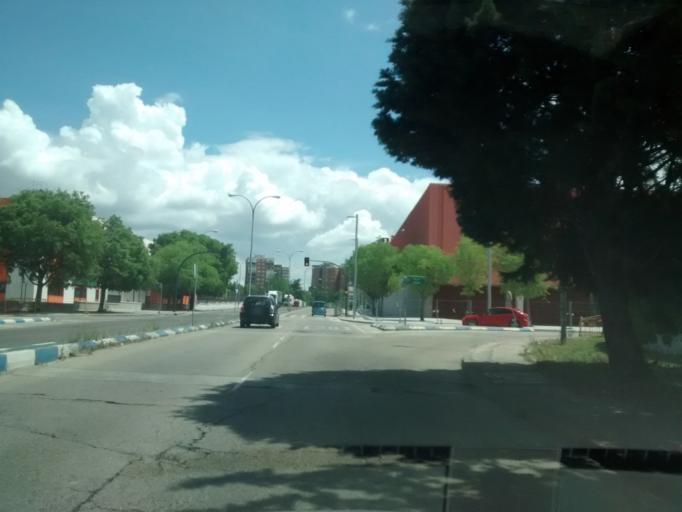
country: ES
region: Madrid
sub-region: Provincia de Madrid
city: Coslada
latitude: 40.4311
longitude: -3.5528
